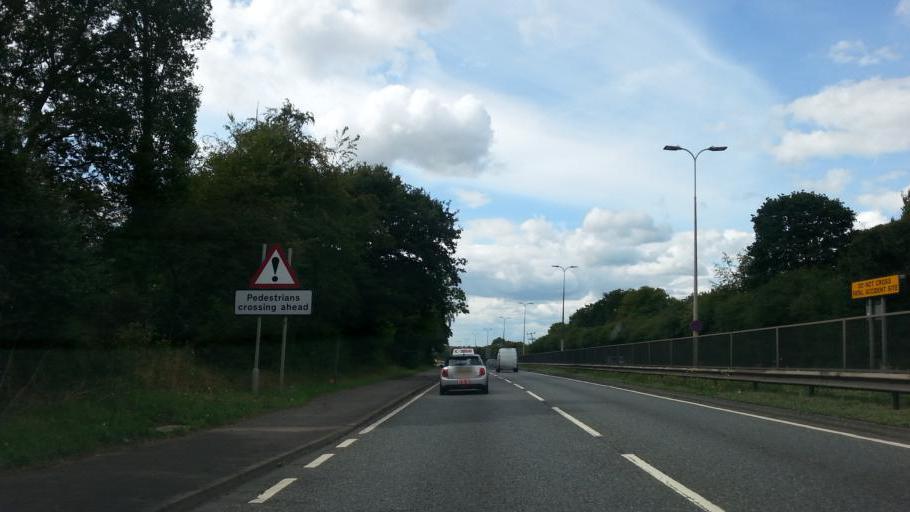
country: GB
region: England
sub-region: Essex
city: Basildon
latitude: 51.5917
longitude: 0.4778
